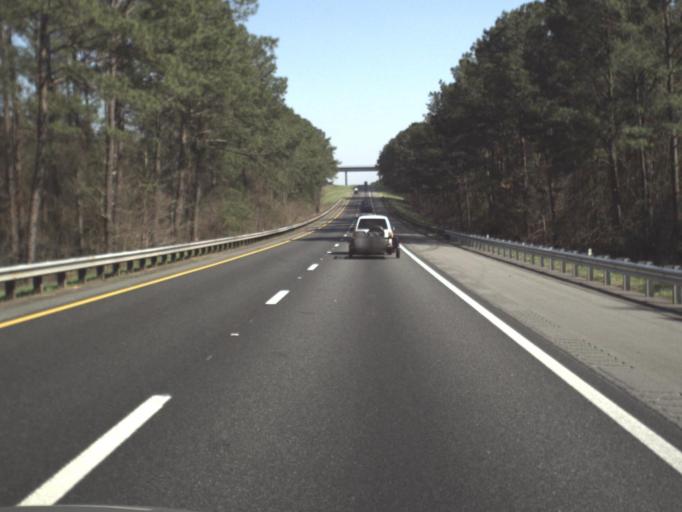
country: US
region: Florida
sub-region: Gadsden County
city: Chattahoochee
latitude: 30.6266
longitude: -84.8534
